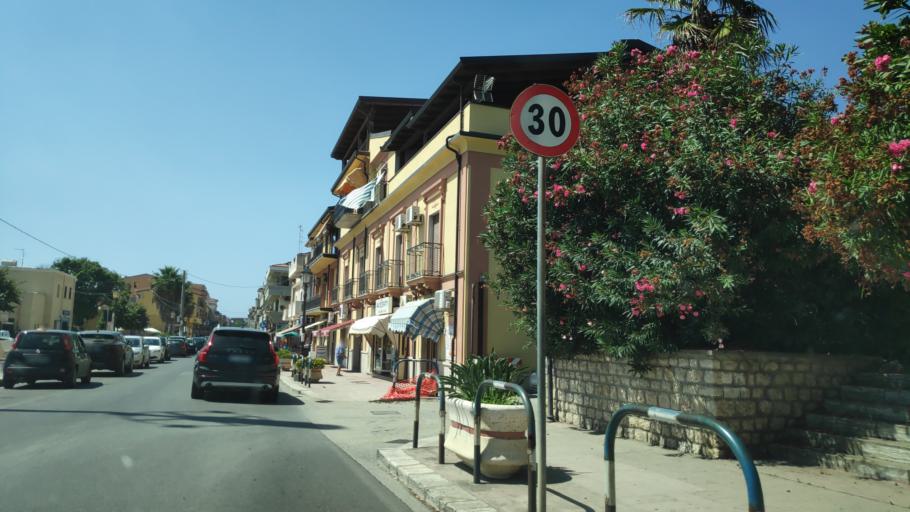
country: IT
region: Calabria
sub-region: Provincia di Reggio Calabria
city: Brancaleone-Marina
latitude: 37.9665
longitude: 16.1034
